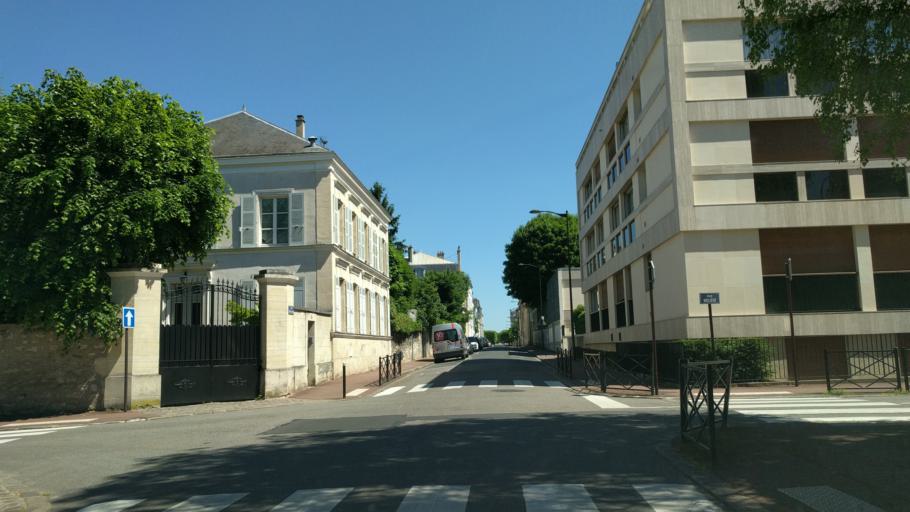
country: FR
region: Ile-de-France
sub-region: Departement des Yvelines
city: Saint-Germain-en-Laye
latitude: 48.9019
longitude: 2.0897
